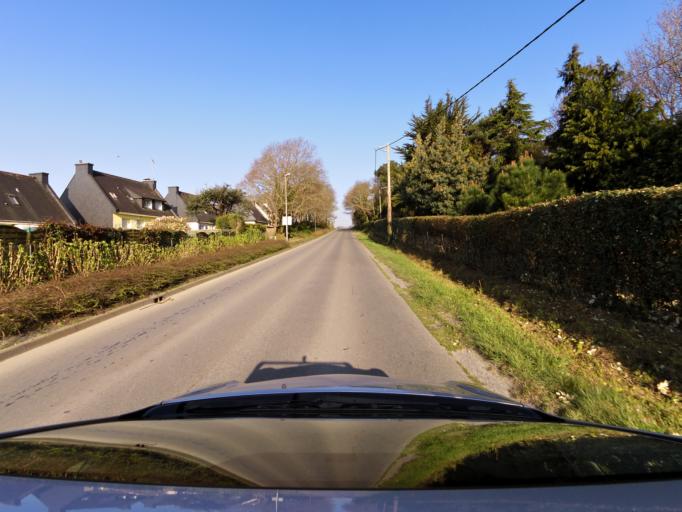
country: FR
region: Brittany
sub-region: Departement du Morbihan
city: Ploemeur
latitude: 47.7378
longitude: -3.4396
